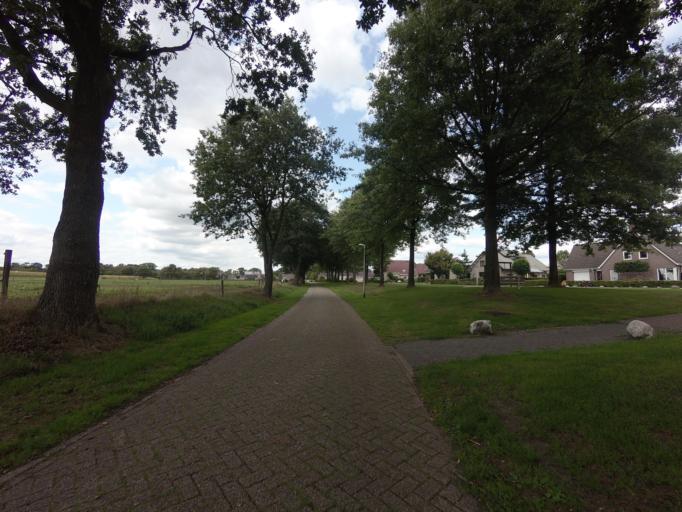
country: NL
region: Drenthe
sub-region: Gemeente De Wolden
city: Ruinen
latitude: 52.7569
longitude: 6.3601
